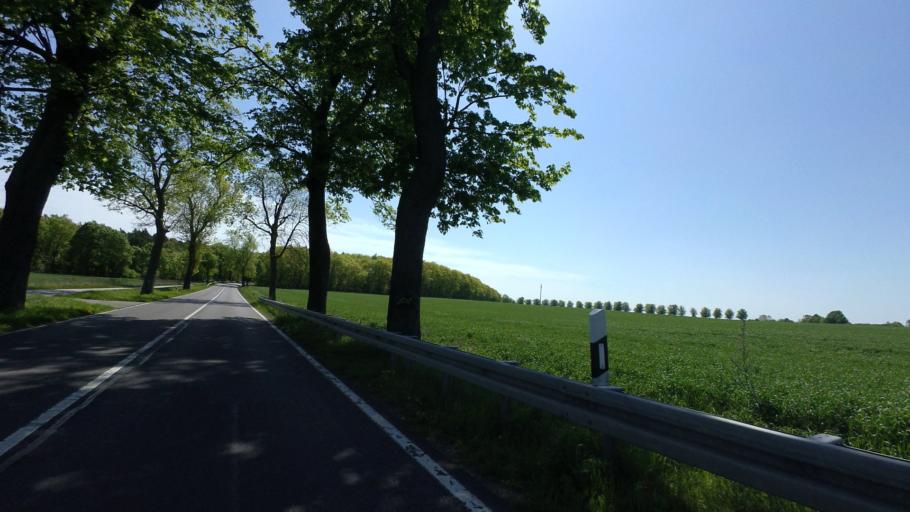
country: DE
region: Brandenburg
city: Schulzendorf
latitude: 52.3481
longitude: 13.5590
